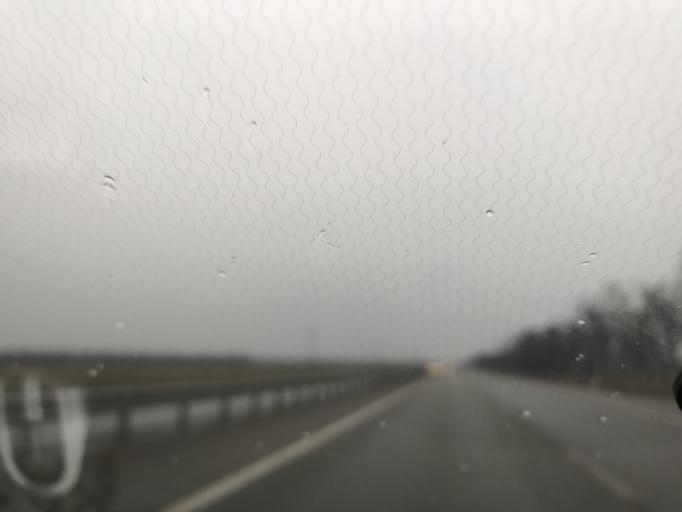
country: RU
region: Krasnodarskiy
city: Kislyakovskaya
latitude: 46.3516
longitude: 39.7711
